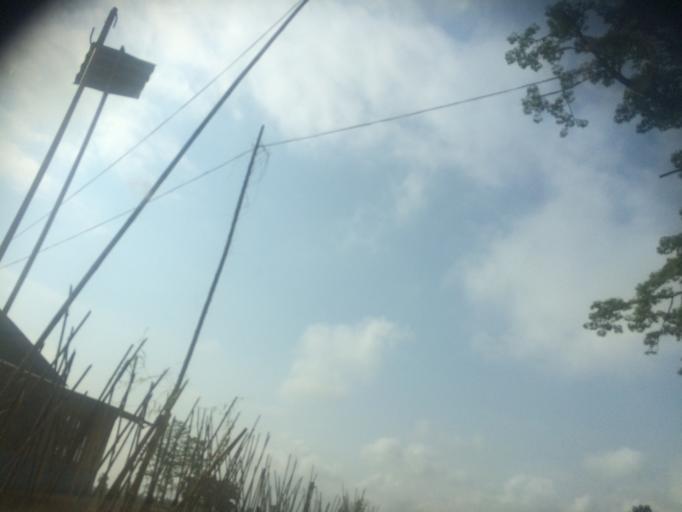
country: MM
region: Bago
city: Pyay
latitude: 18.6765
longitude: 95.0514
